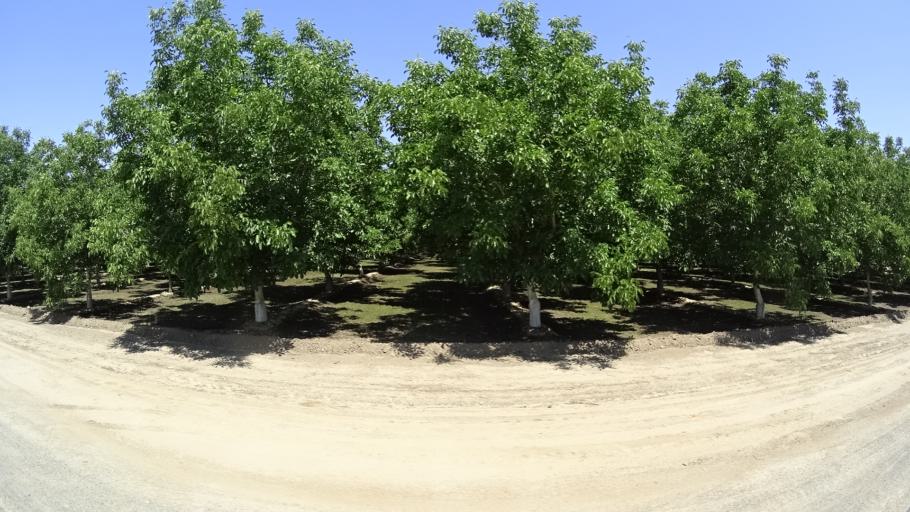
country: US
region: California
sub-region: Kings County
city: Lucerne
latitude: 36.3572
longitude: -119.6781
